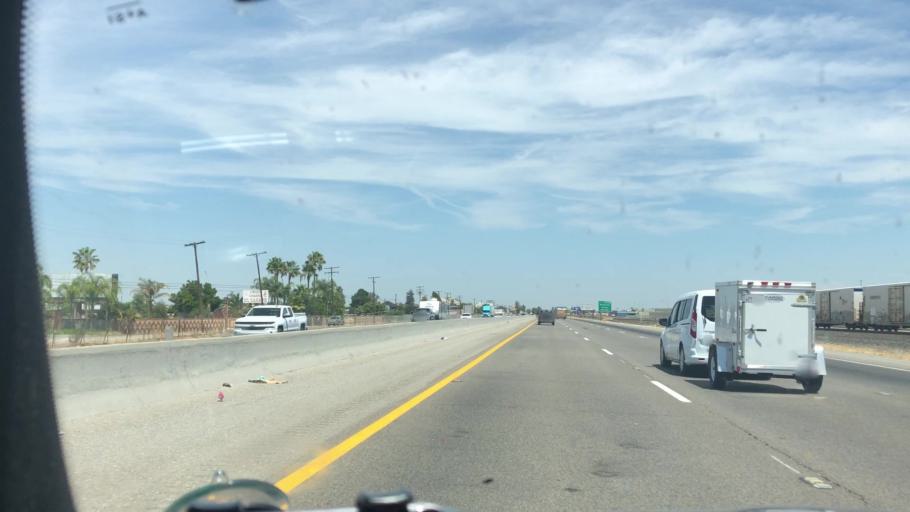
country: US
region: California
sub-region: Kern County
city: Delano
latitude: 35.7330
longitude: -119.2399
